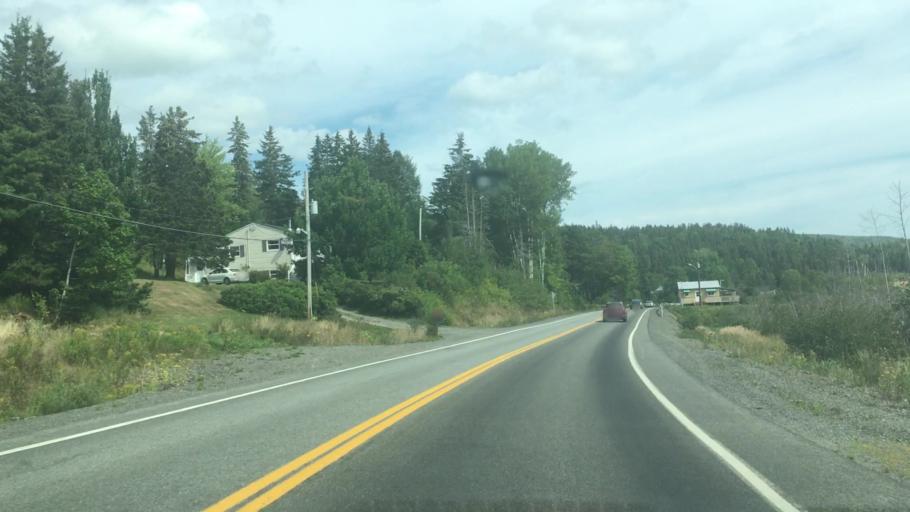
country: CA
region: Nova Scotia
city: Sydney Mines
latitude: 46.2646
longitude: -60.6239
